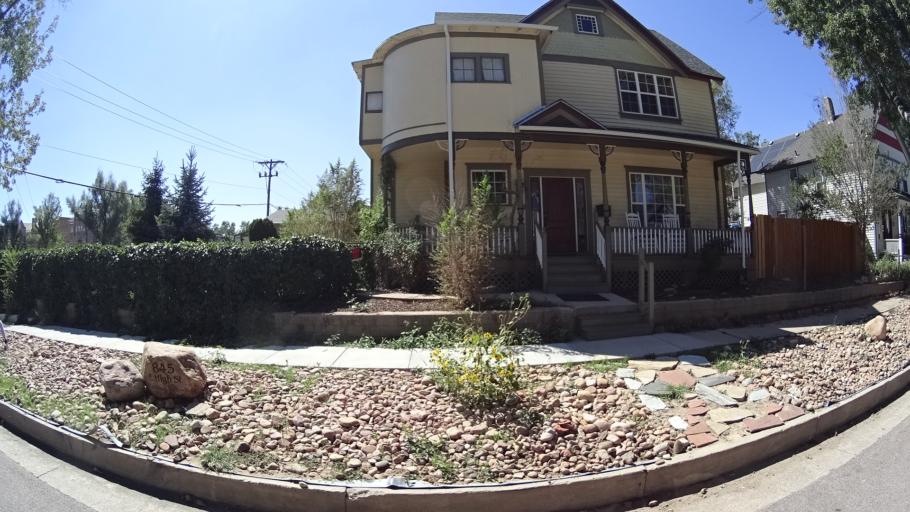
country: US
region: Colorado
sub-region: El Paso County
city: Colorado Springs
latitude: 38.8358
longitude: -104.8084
